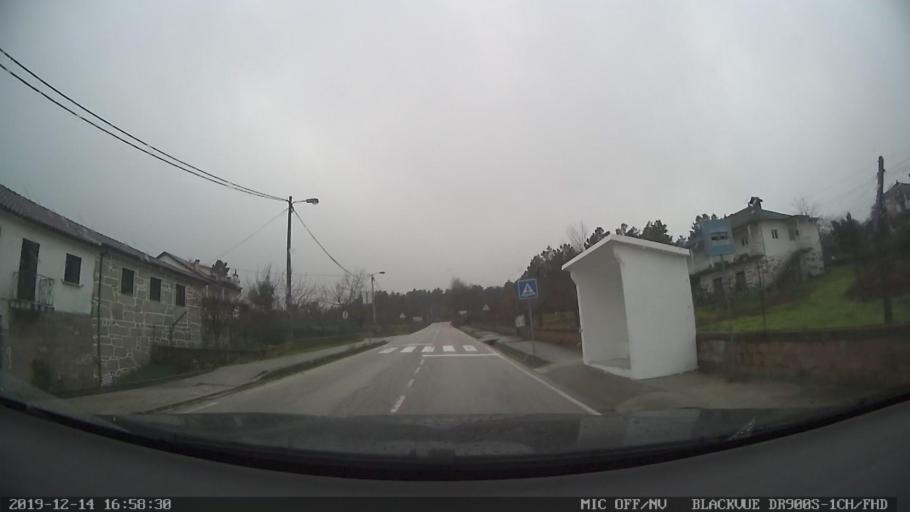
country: PT
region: Vila Real
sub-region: Murca
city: Murca
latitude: 41.4367
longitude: -7.5532
